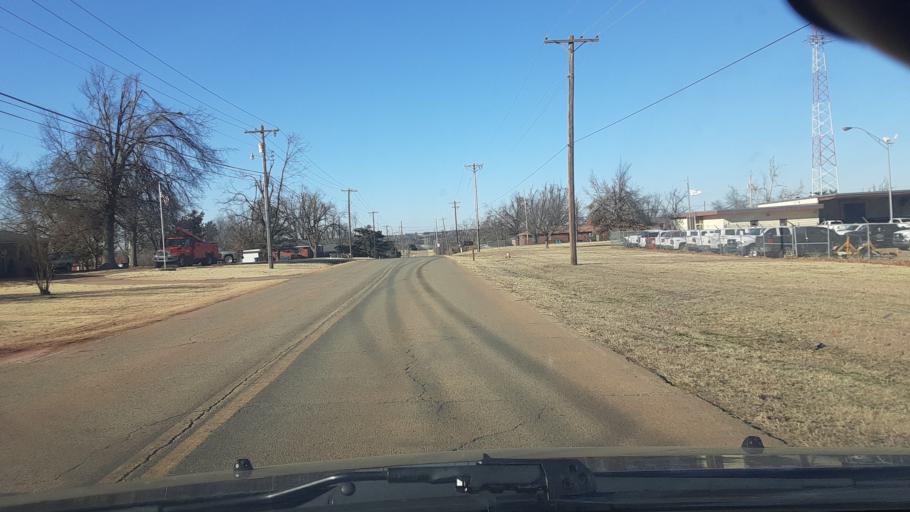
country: US
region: Oklahoma
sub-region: Logan County
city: Guthrie
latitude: 35.8562
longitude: -97.4290
